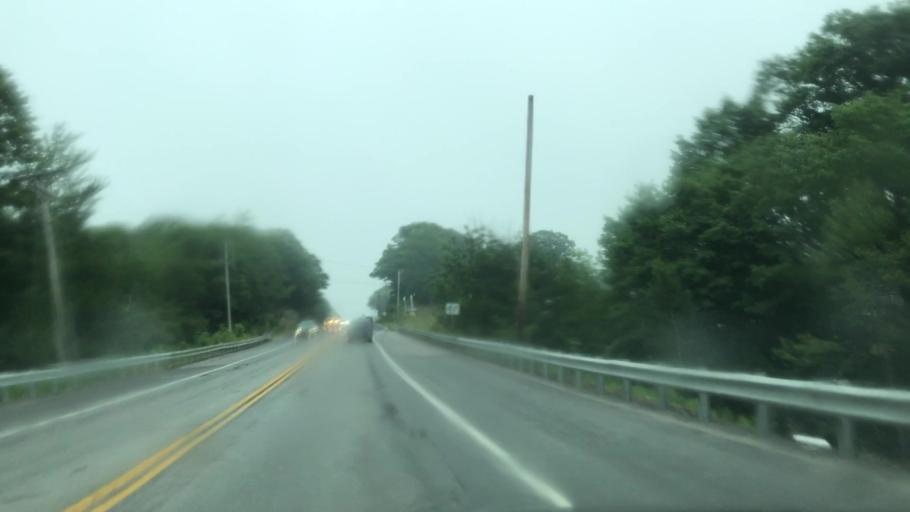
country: US
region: Maine
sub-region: Lincoln County
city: Waldoboro
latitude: 44.1024
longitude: -69.3775
